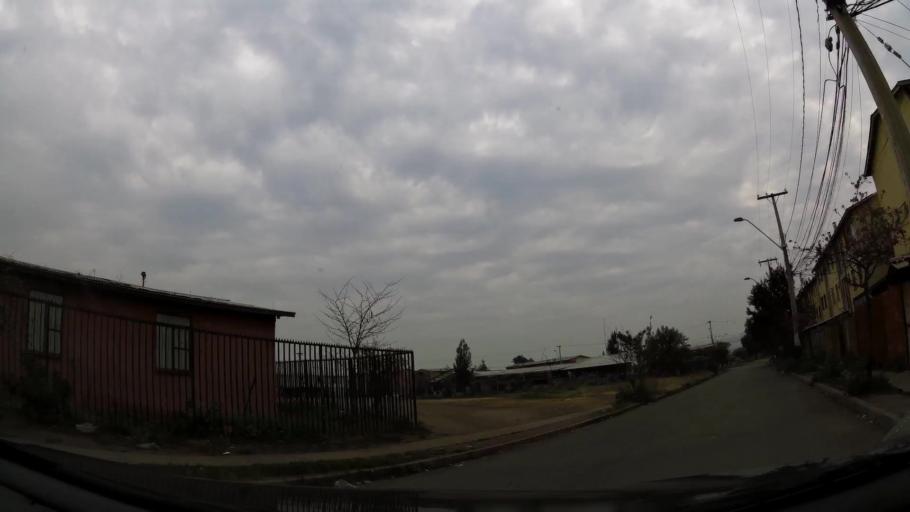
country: CL
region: Santiago Metropolitan
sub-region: Provincia de Chacabuco
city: Chicureo Abajo
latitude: -33.1877
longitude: -70.6639
